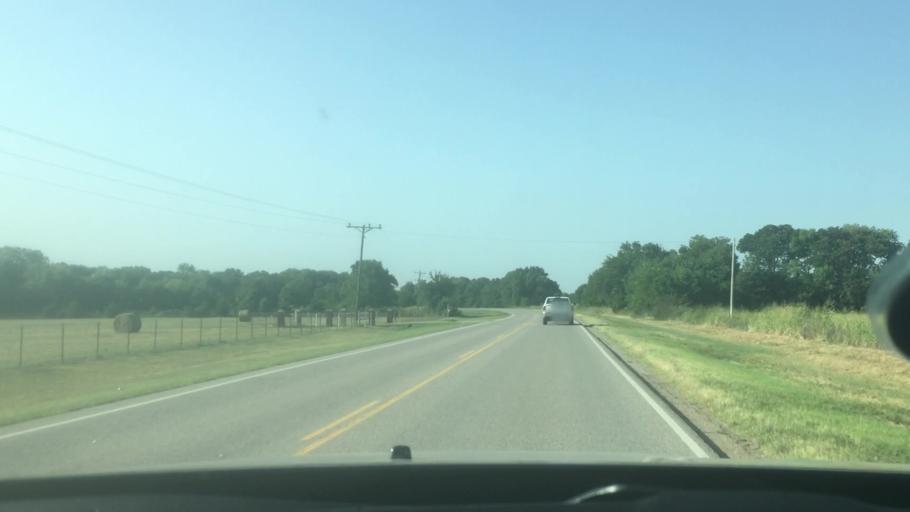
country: US
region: Oklahoma
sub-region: Bryan County
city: Durant
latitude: 34.1805
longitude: -96.4163
